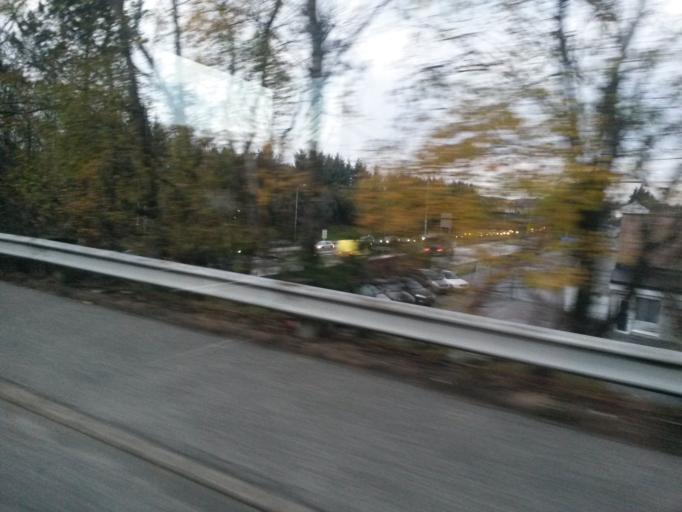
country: NO
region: Rogaland
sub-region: Stavanger
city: Stavanger
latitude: 58.9445
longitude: 5.7258
